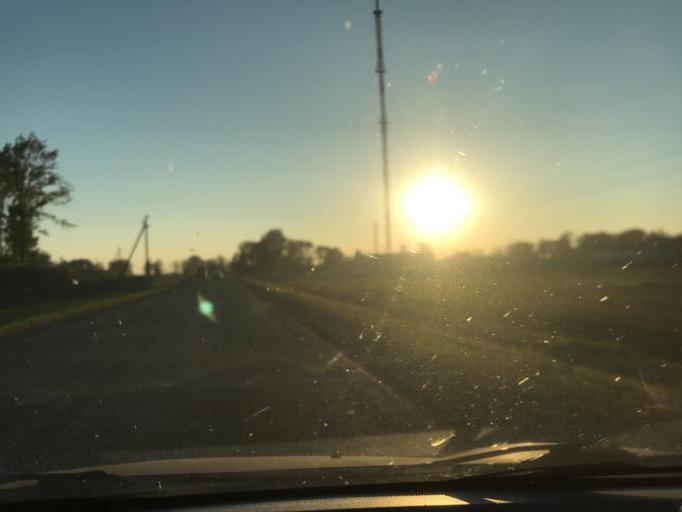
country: BY
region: Gomel
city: Brahin
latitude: 51.7989
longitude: 30.2651
